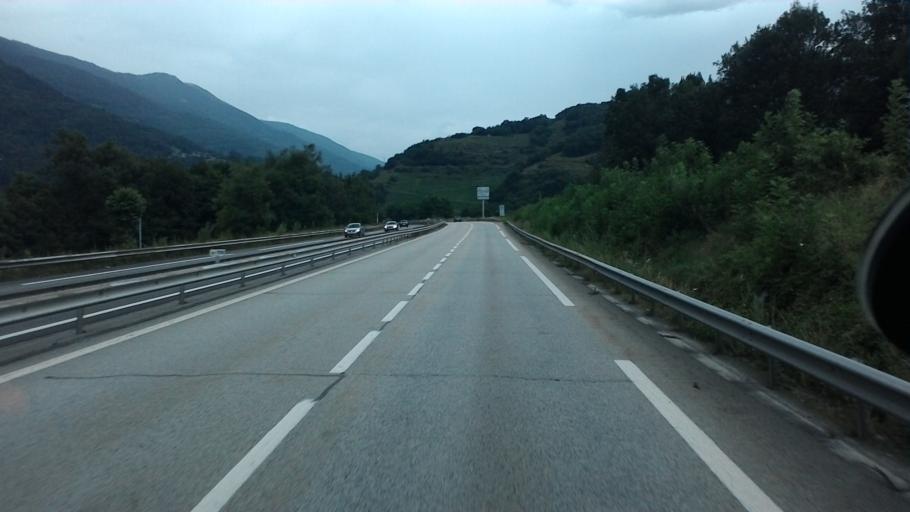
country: FR
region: Rhone-Alpes
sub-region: Departement de la Savoie
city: La Bathie
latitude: 45.5869
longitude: 6.4531
